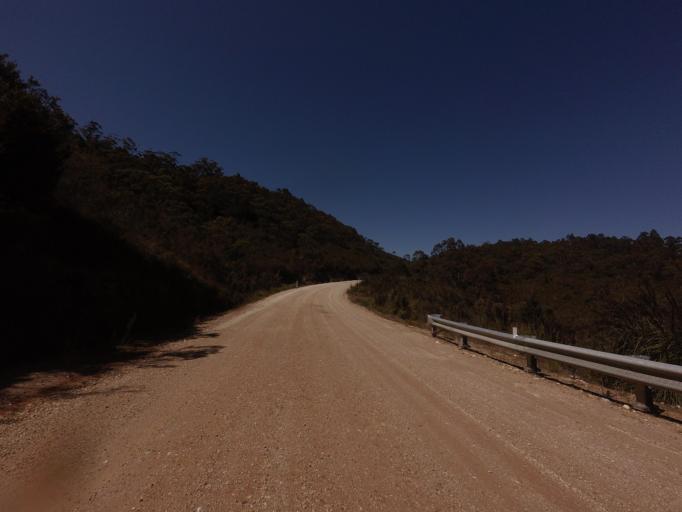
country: AU
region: Tasmania
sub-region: Huon Valley
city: Geeveston
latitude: -42.9822
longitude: 146.3641
